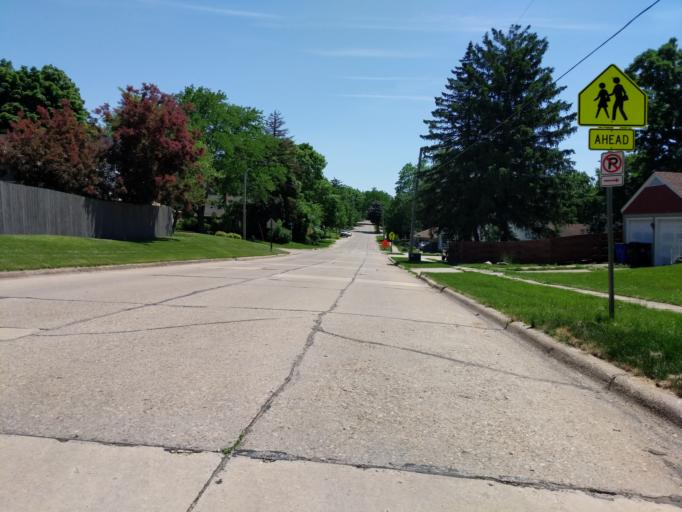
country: US
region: Iowa
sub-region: Linn County
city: Cedar Rapids
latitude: 42.0155
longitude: -91.6410
